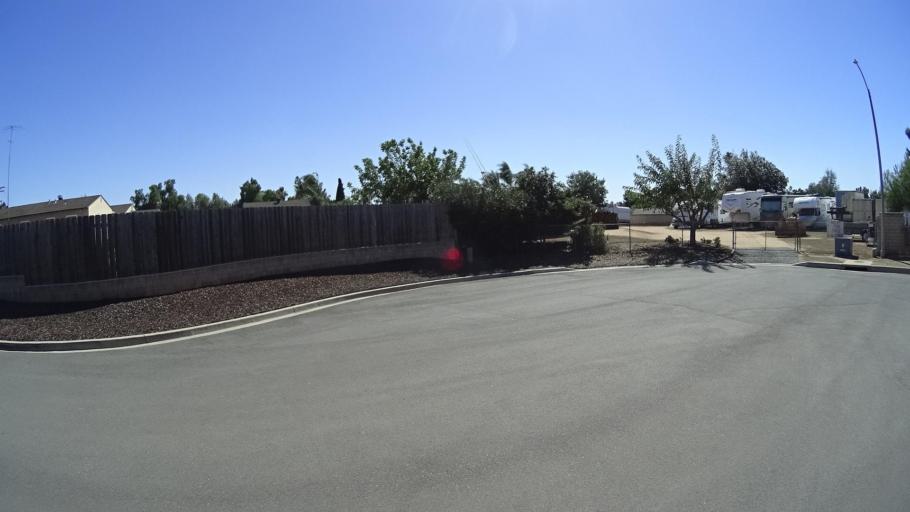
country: US
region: California
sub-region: San Diego County
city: Bonita
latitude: 32.6574
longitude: -117.0550
